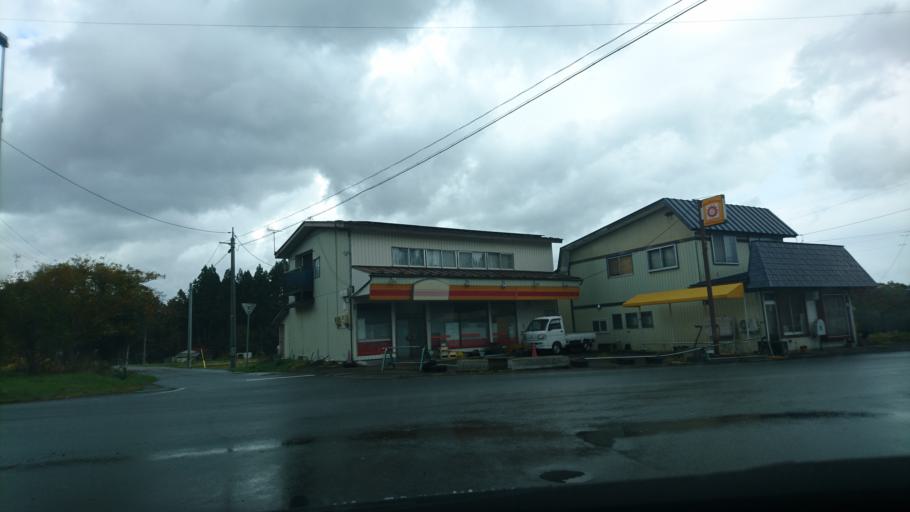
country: JP
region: Iwate
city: Shizukuishi
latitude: 39.6483
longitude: 140.9517
